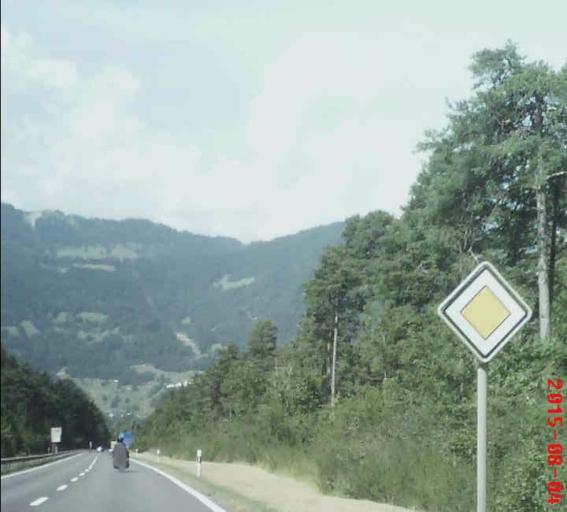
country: CH
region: Grisons
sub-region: Landquart District
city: Malans
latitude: 46.9701
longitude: 9.5923
